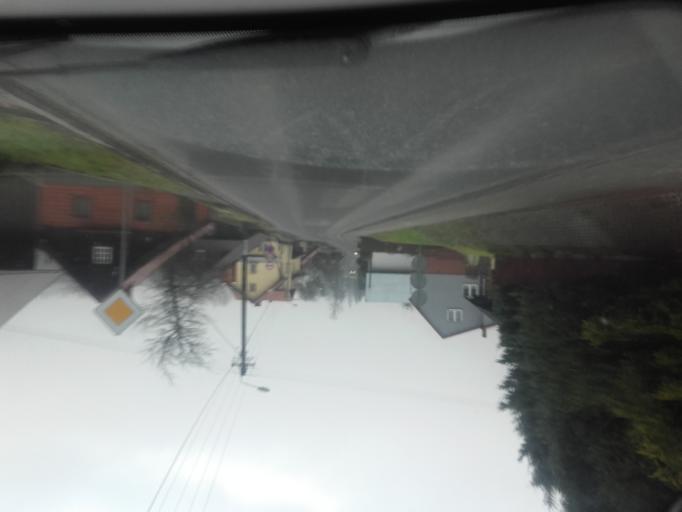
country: PL
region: Silesian Voivodeship
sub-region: Powiat cieszynski
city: Istebna
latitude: 49.5631
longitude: 18.9065
